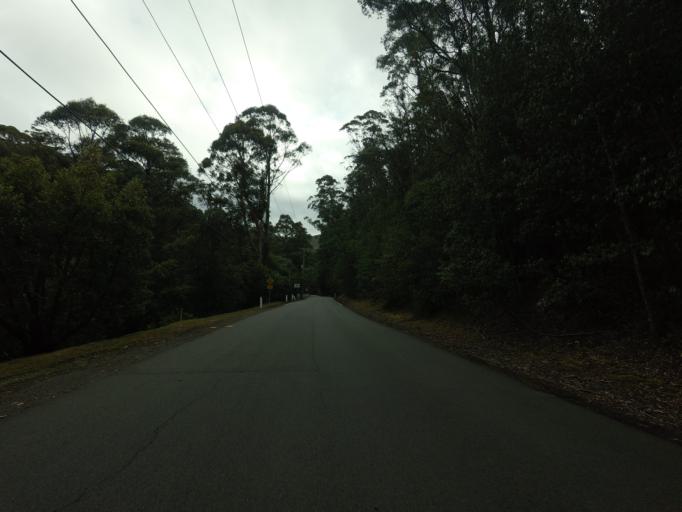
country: AU
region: Tasmania
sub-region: Hobart
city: Dynnyrne
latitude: -42.9070
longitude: 147.2659
